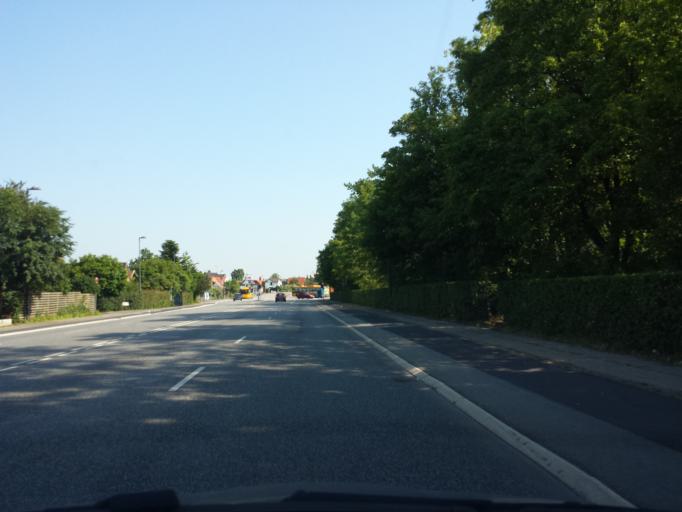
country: DK
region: Capital Region
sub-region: Ballerup Kommune
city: Ballerup
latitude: 55.7222
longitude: 12.3563
